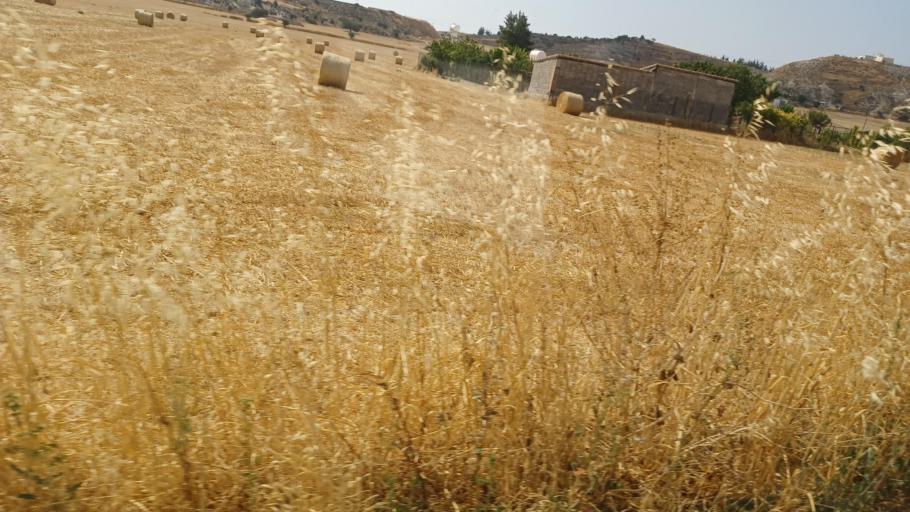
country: CY
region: Larnaka
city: Aradippou
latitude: 34.9202
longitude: 33.5376
